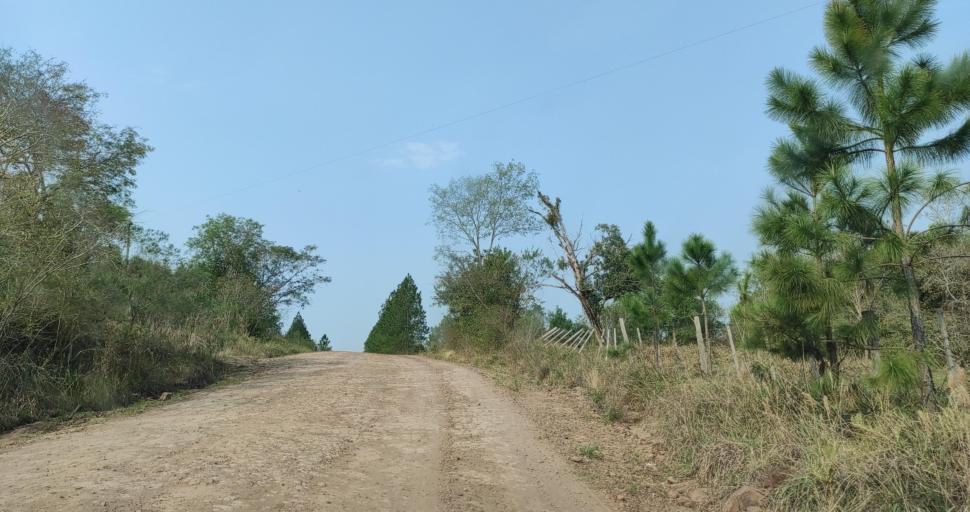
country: AR
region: Misiones
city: Cerro Azul
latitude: -27.6263
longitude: -55.5425
